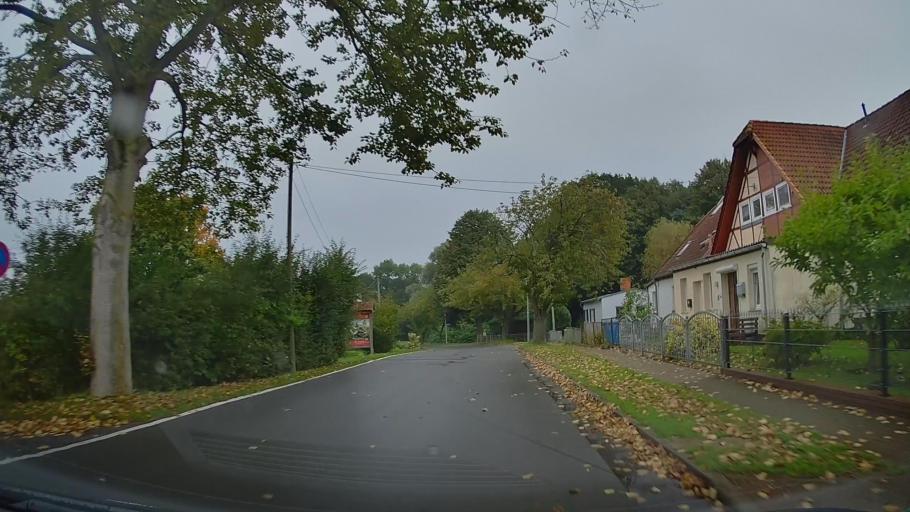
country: DE
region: Mecklenburg-Vorpommern
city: Kalkhorst
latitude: 53.9972
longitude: 11.0433
